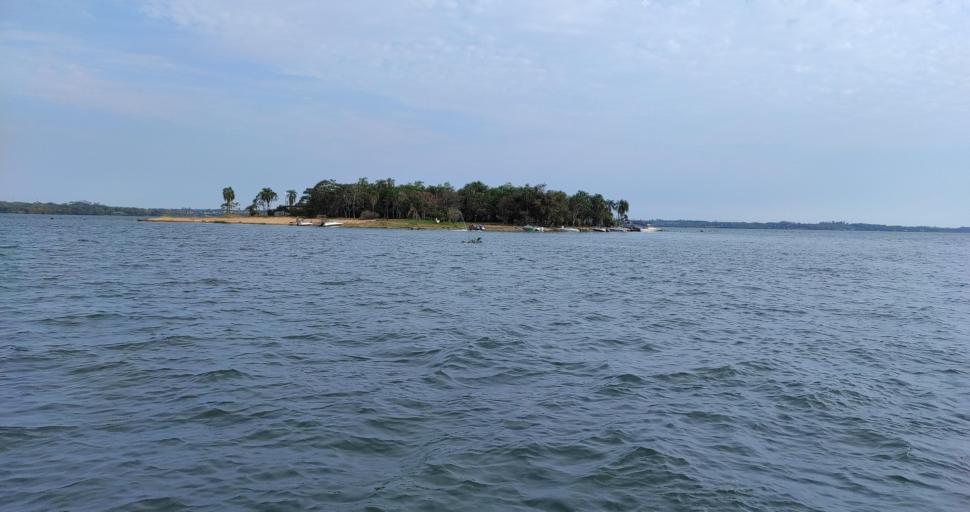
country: PY
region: Itapua
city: San Juan del Parana
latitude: -27.3382
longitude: -55.9505
